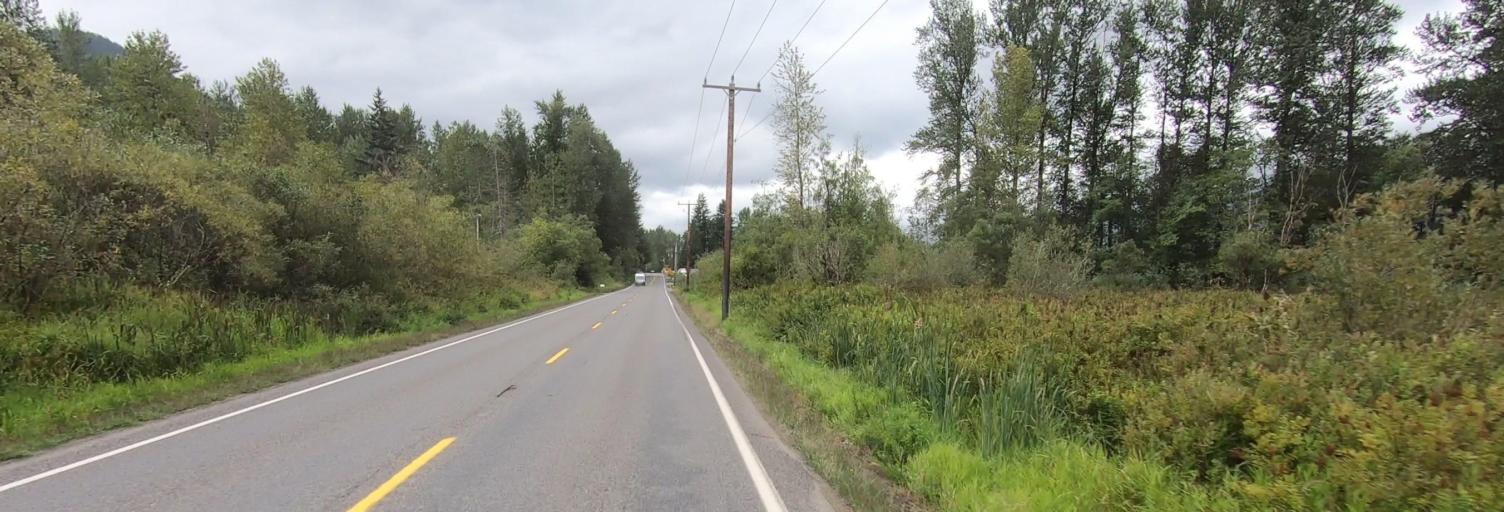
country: US
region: Washington
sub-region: Whatcom County
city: Peaceful Valley
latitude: 48.7934
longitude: -122.1905
